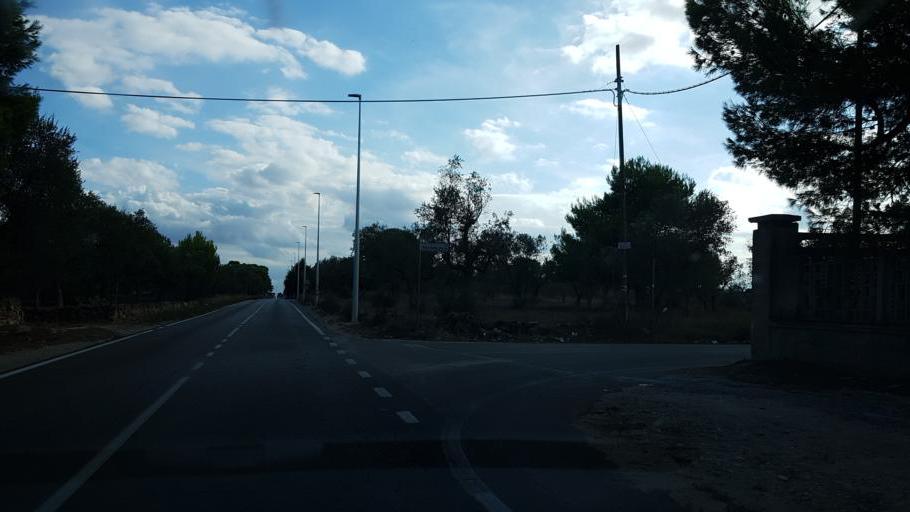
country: IT
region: Apulia
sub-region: Provincia di Lecce
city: Nardo
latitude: 40.1432
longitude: 18.0186
